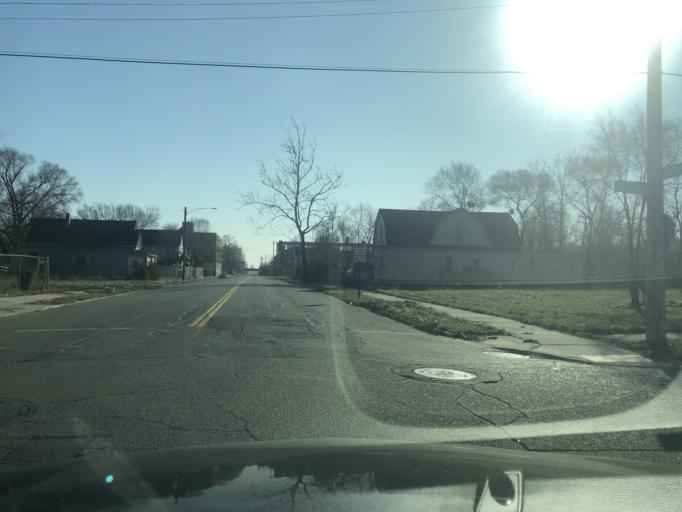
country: US
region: Michigan
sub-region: Wayne County
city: Detroit
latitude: 42.3358
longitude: -83.1046
